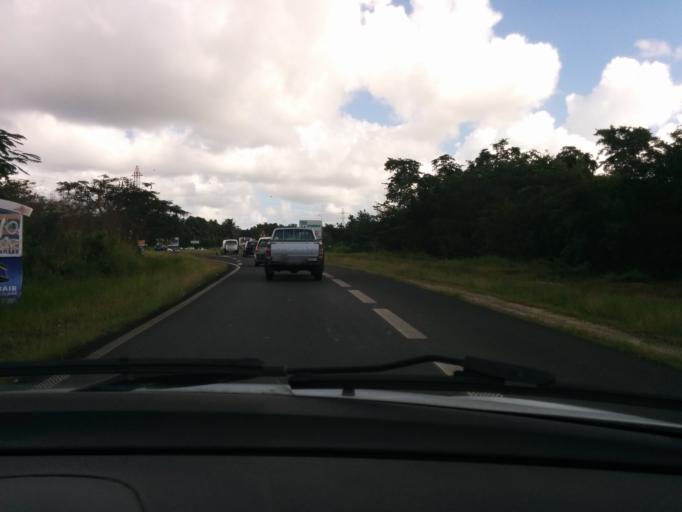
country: GP
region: Guadeloupe
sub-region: Guadeloupe
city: Pointe-a-Pitre
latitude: 16.2525
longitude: -61.5523
